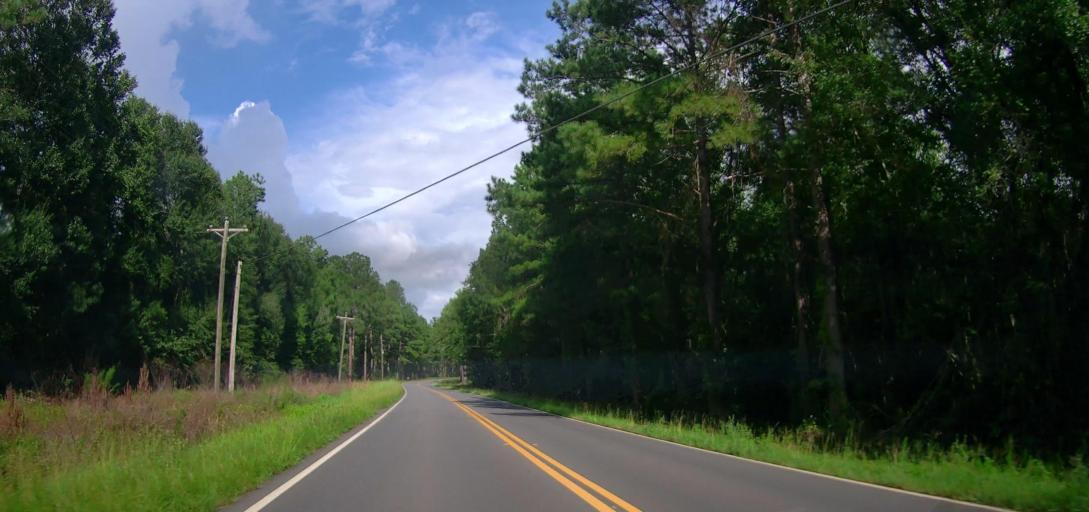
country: US
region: Georgia
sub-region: Coffee County
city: Douglas
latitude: 31.4513
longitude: -82.8846
